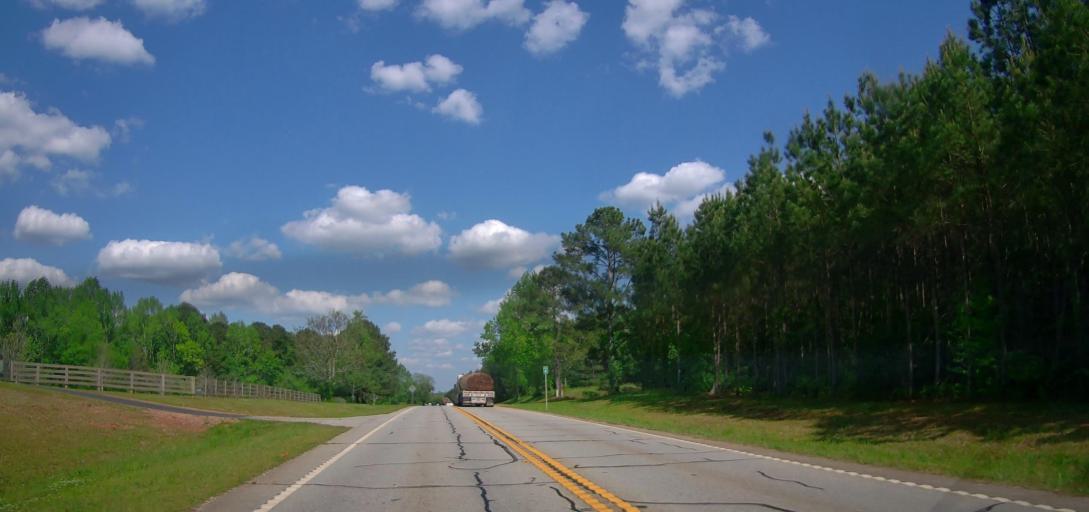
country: US
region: Georgia
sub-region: Greene County
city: Greensboro
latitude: 33.5710
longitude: -83.2332
